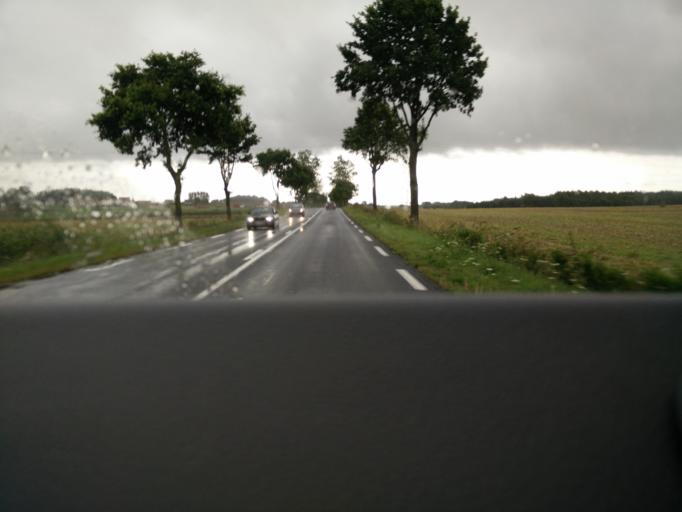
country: FR
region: Nord-Pas-de-Calais
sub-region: Departement du Pas-de-Calais
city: Savy-Berlette
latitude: 50.3523
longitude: 2.5048
